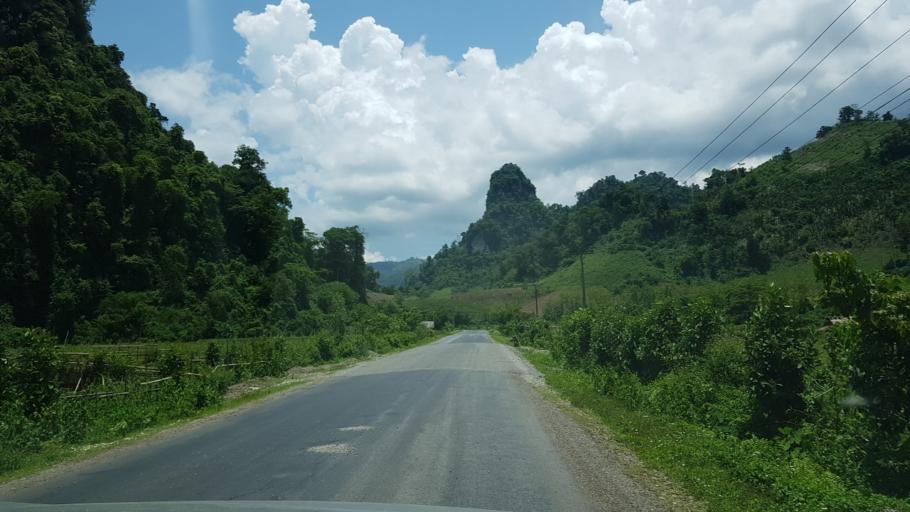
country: LA
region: Vientiane
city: Muang Kasi
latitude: 19.1237
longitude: 102.2563
